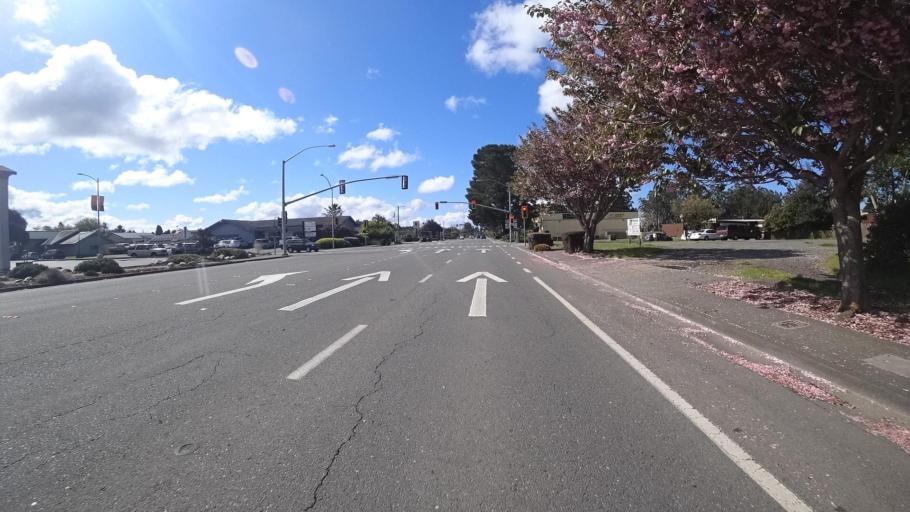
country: US
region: California
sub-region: Humboldt County
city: McKinleyville
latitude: 40.9447
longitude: -124.1011
